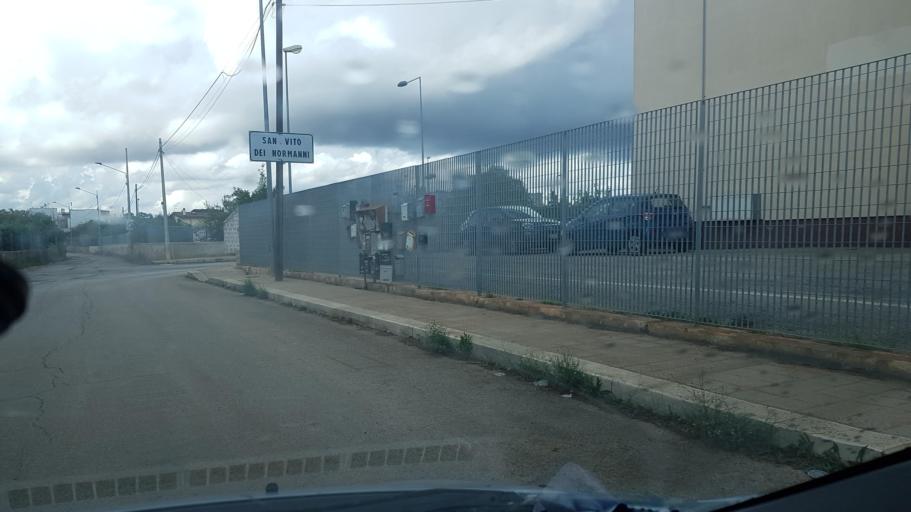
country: IT
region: Apulia
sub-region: Provincia di Brindisi
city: San Vito dei Normanni
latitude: 40.6540
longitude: 17.7192
